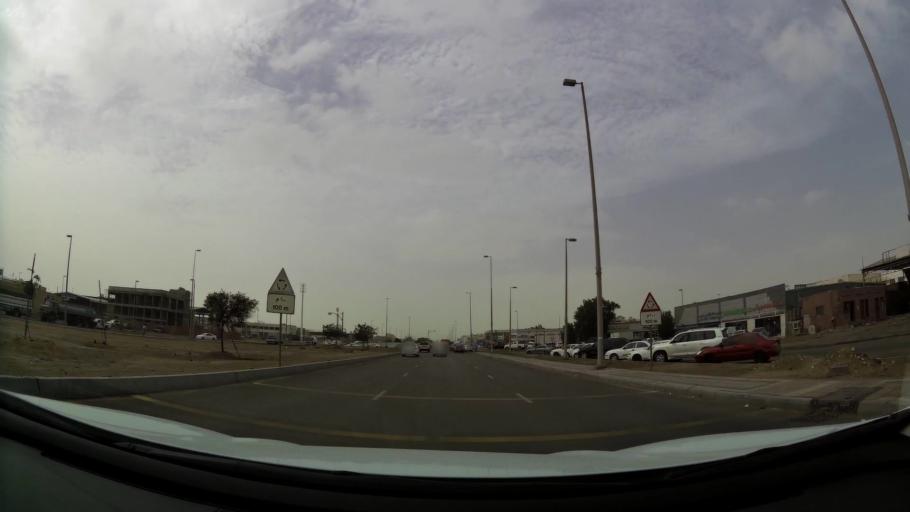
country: AE
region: Abu Dhabi
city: Abu Dhabi
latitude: 24.3689
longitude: 54.5128
